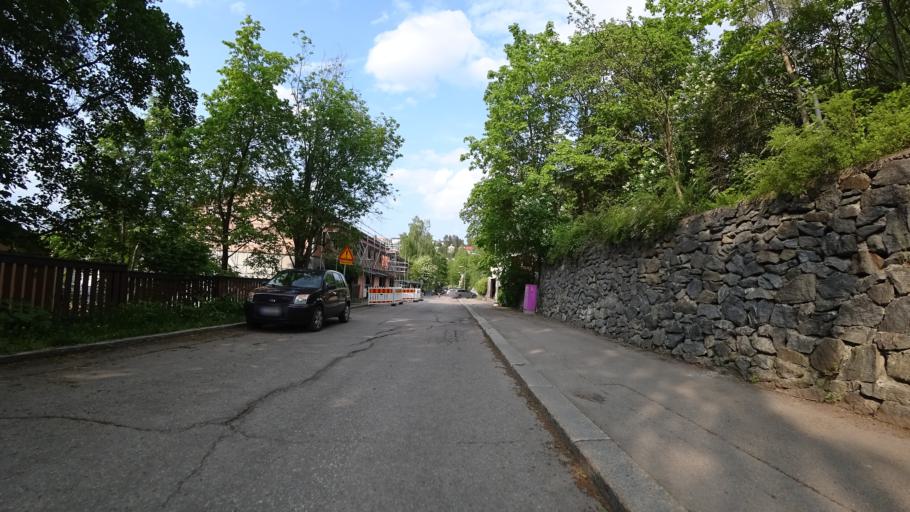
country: FI
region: Pirkanmaa
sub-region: Tampere
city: Tampere
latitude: 61.4969
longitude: 23.7130
